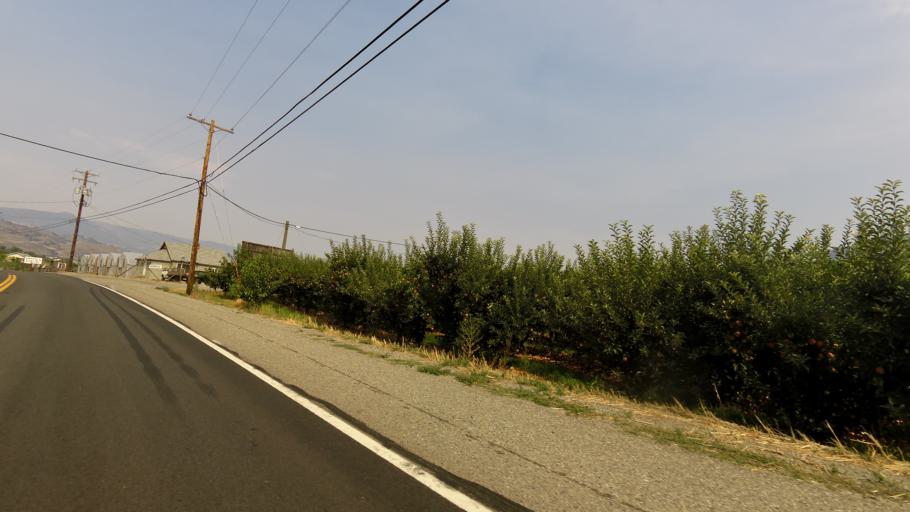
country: CA
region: British Columbia
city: Osoyoos
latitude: 49.0419
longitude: -119.4847
